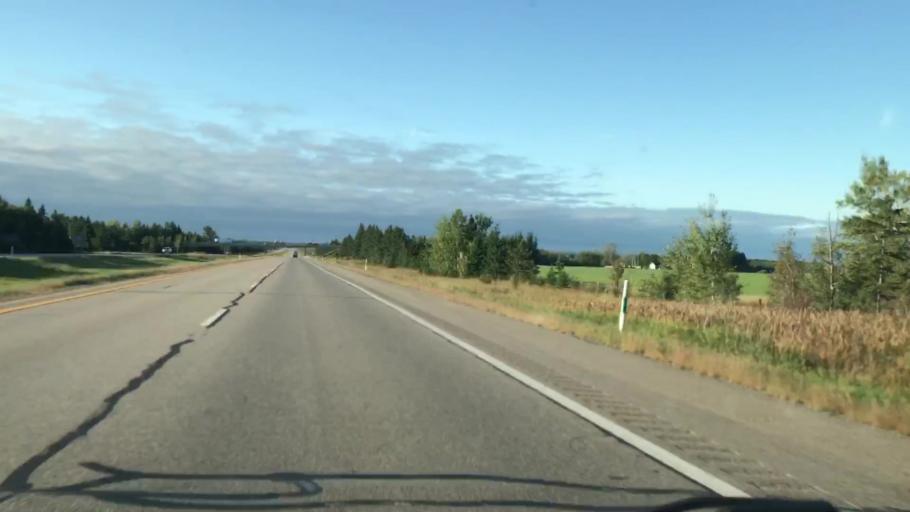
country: US
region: Michigan
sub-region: Chippewa County
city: Sault Ste. Marie
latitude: 46.4237
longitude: -84.3936
